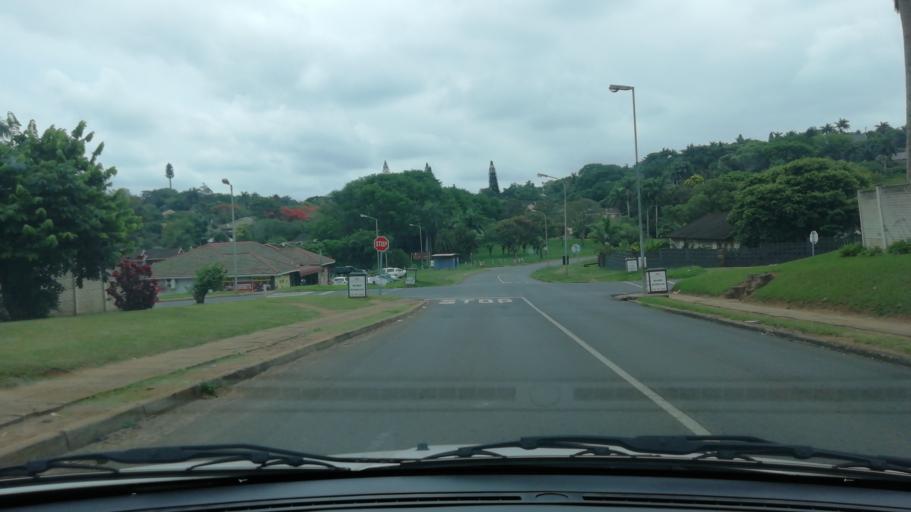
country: ZA
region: KwaZulu-Natal
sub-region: uThungulu District Municipality
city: Empangeni
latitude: -28.7582
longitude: 31.8932
